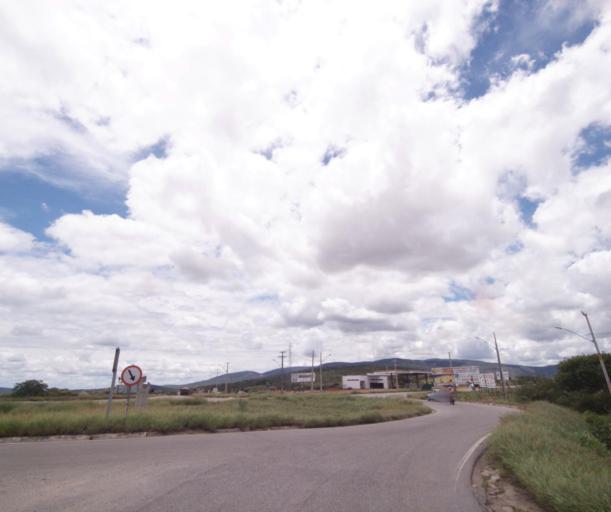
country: BR
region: Bahia
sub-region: Brumado
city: Brumado
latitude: -14.2147
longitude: -41.6456
